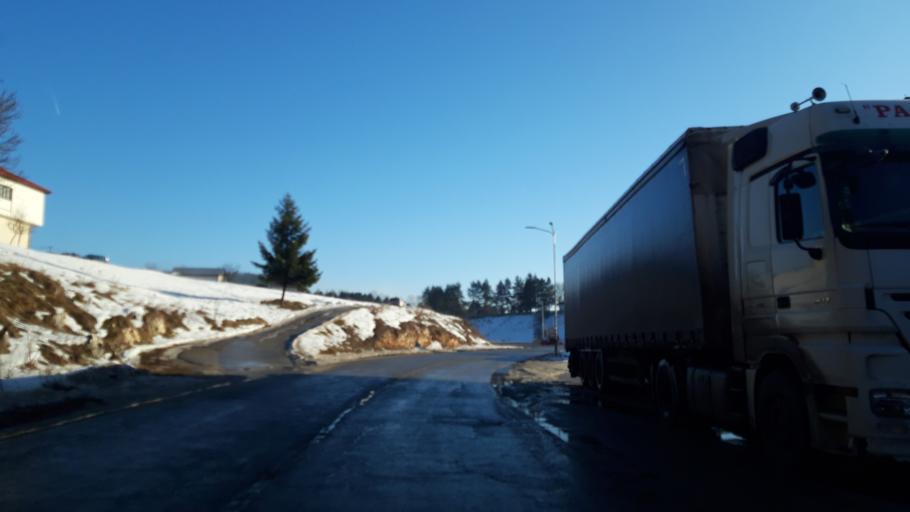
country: BA
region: Republika Srpska
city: Sokolac
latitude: 43.9364
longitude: 18.8011
